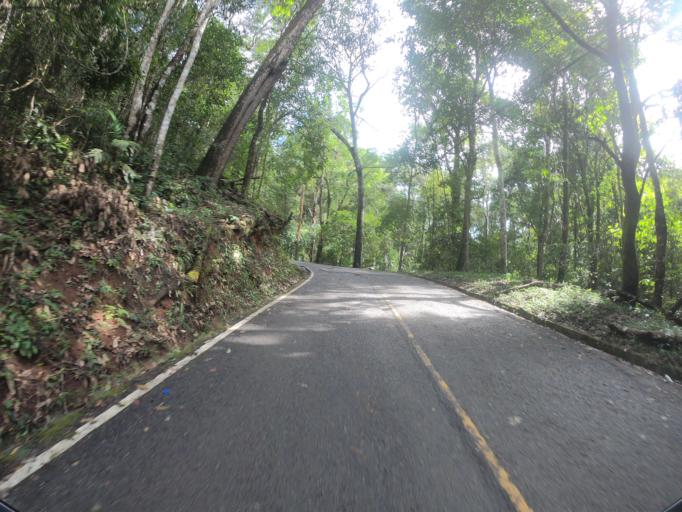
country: TH
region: Chiang Mai
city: Chiang Mai
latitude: 18.8099
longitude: 98.8906
